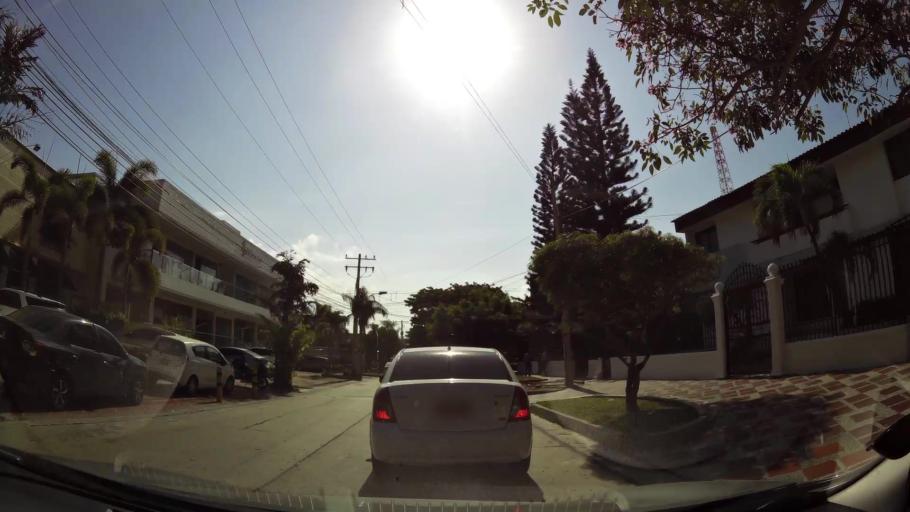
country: CO
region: Atlantico
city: Barranquilla
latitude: 10.9993
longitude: -74.8179
